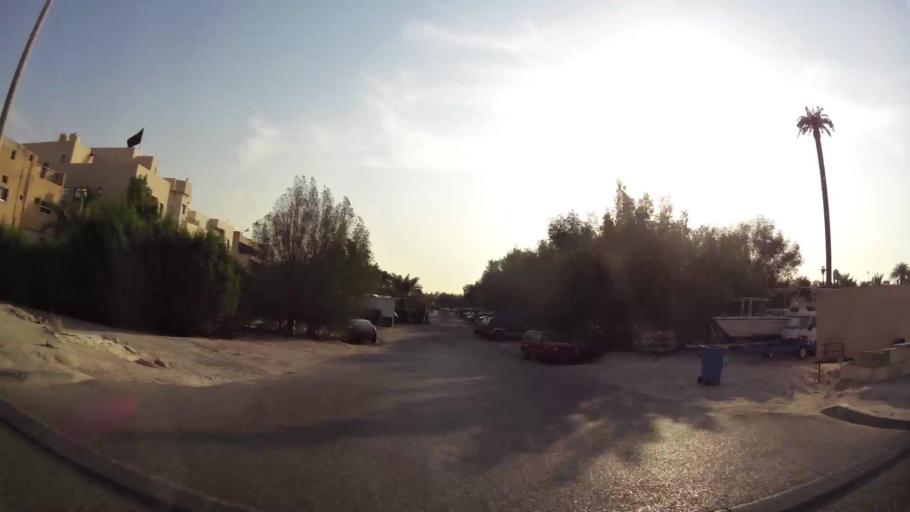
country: KW
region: Muhafazat Hawalli
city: Ar Rumaythiyah
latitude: 29.3184
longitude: 48.0730
